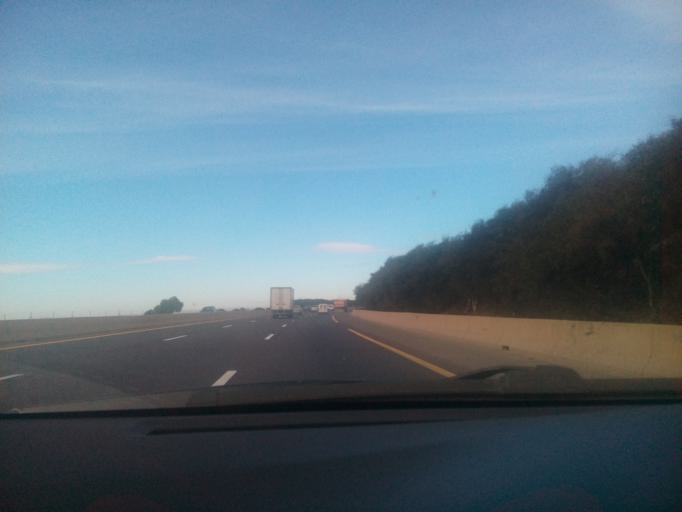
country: DZ
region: Oran
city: Es Senia
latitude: 35.5788
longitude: -0.5669
